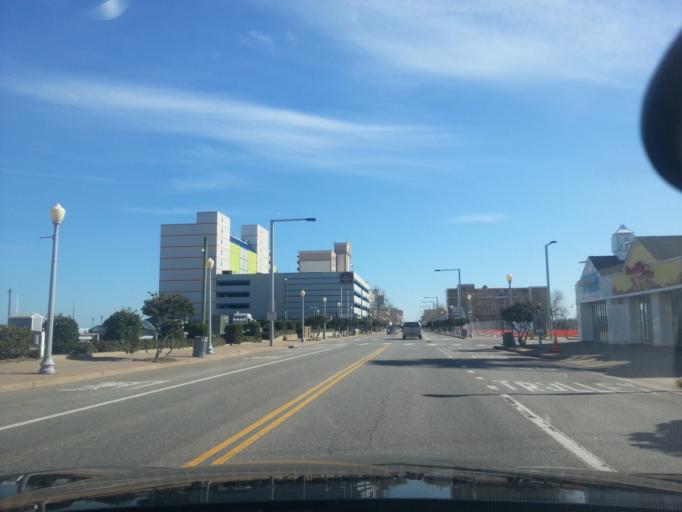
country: US
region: Virginia
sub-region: City of Virginia Beach
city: Virginia Beach
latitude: 36.8439
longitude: -75.9739
